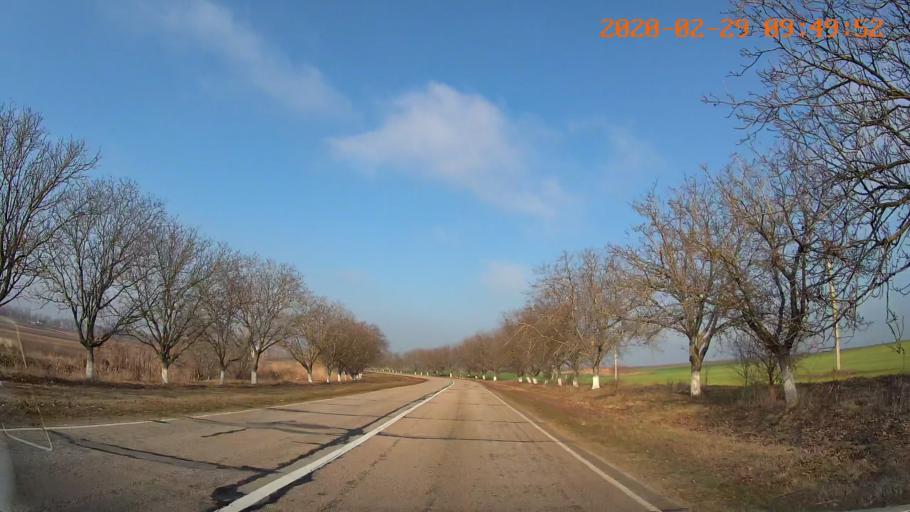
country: MD
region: Telenesti
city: Crasnoe
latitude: 46.7001
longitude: 29.7657
